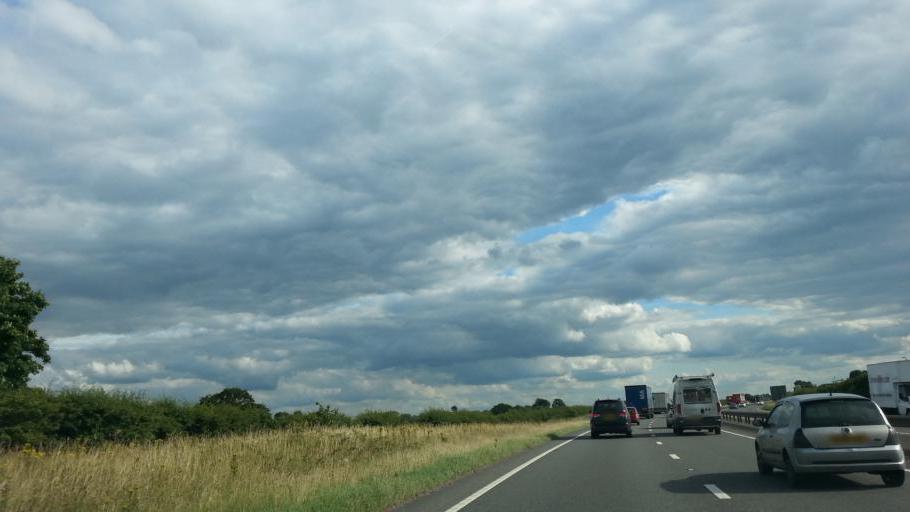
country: GB
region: England
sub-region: Nottinghamshire
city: South Collingham
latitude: 53.1449
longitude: -0.8037
